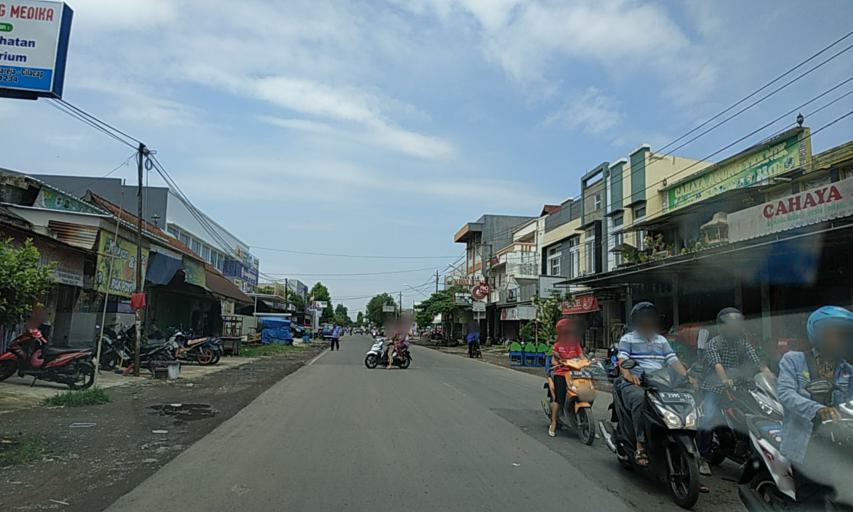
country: ID
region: Central Java
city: Sidareja
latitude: -7.4854
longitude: 108.7917
